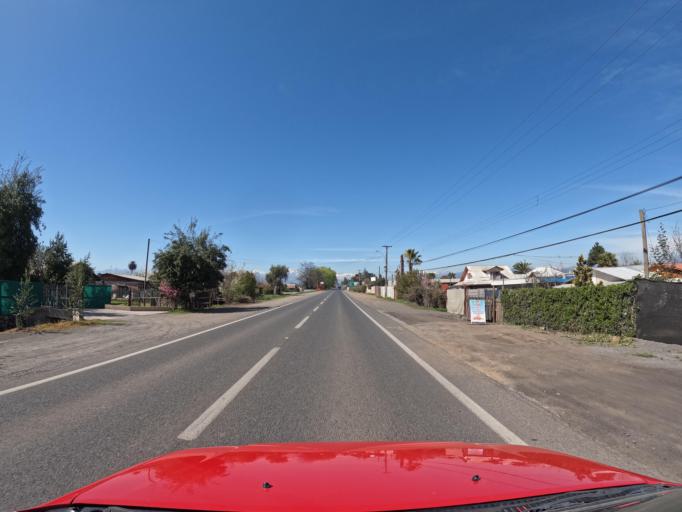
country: CL
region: Maule
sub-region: Provincia de Curico
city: Teno
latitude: -34.9621
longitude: -71.0855
